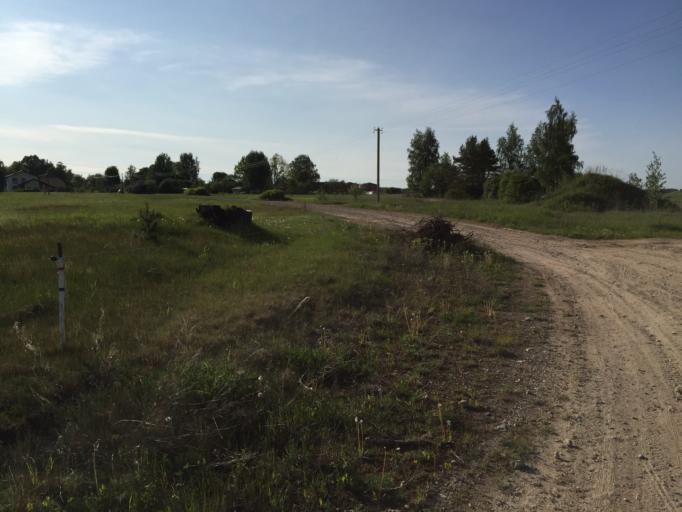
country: LV
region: Kekava
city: Kekava
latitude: 56.8242
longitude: 24.2740
